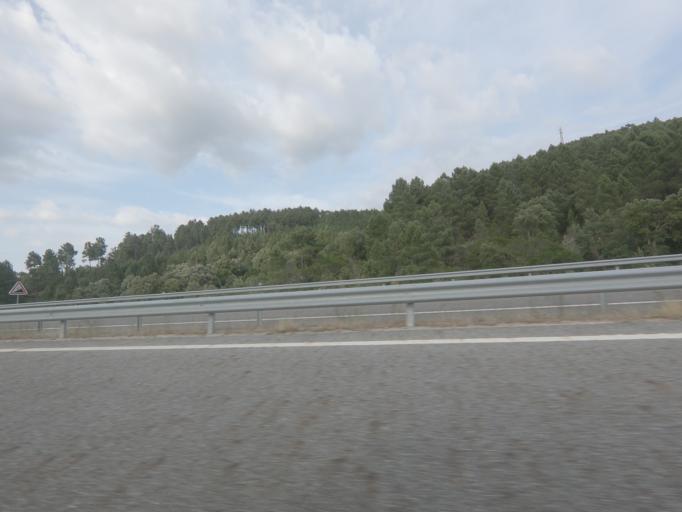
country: PT
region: Vila Real
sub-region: Boticas
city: Boticas
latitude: 41.6773
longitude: -7.5664
